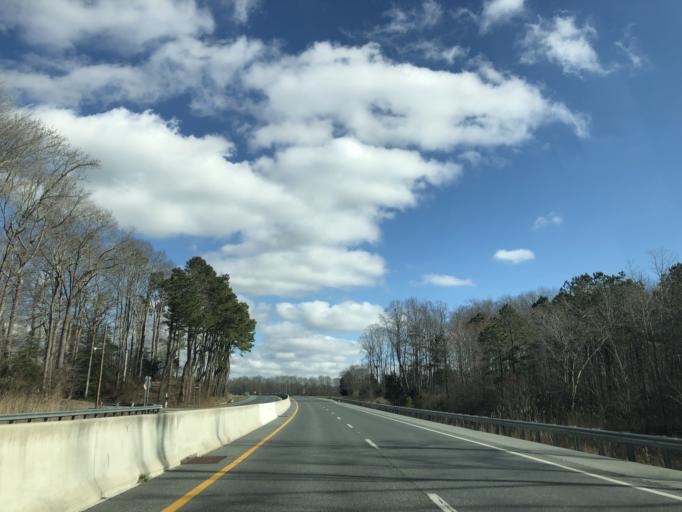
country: US
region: Maryland
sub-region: Worcester County
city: Berlin
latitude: 38.2536
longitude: -75.2669
